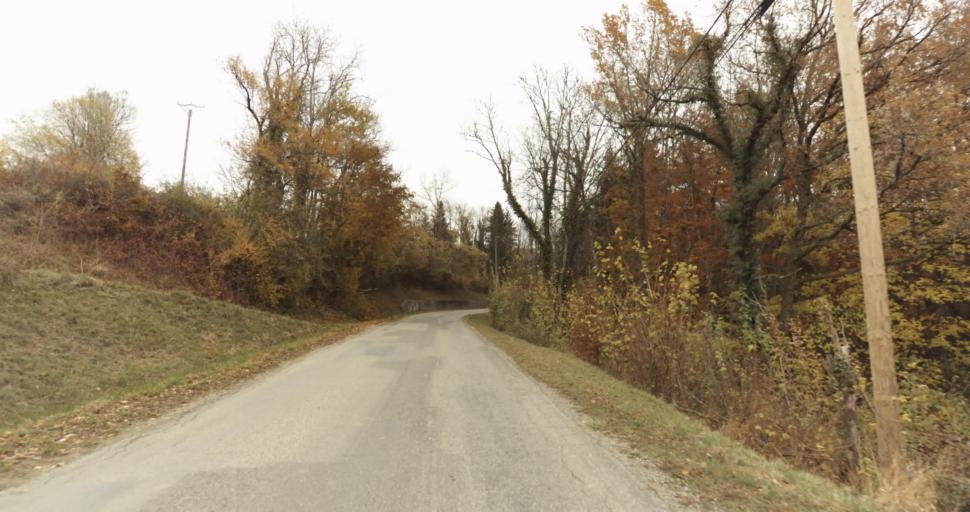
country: FR
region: Rhone-Alpes
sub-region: Departement de la Haute-Savoie
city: Saint-Martin-Bellevue
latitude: 45.9825
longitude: 6.1810
